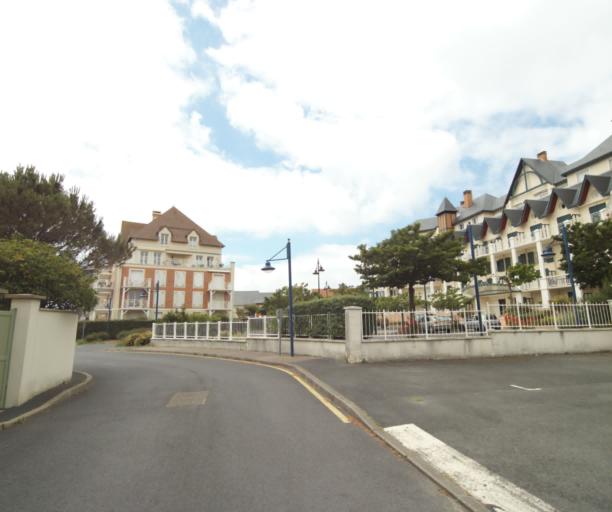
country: FR
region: Lower Normandy
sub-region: Departement du Calvados
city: Dives-sur-Mer
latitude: 49.2949
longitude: -0.0977
